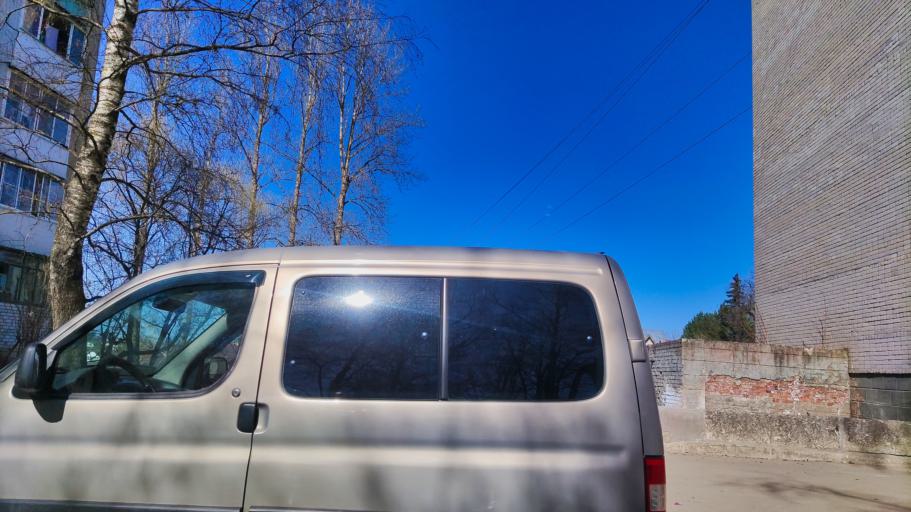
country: RU
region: Tverskaya
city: Rzhev
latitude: 56.2616
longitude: 34.3465
